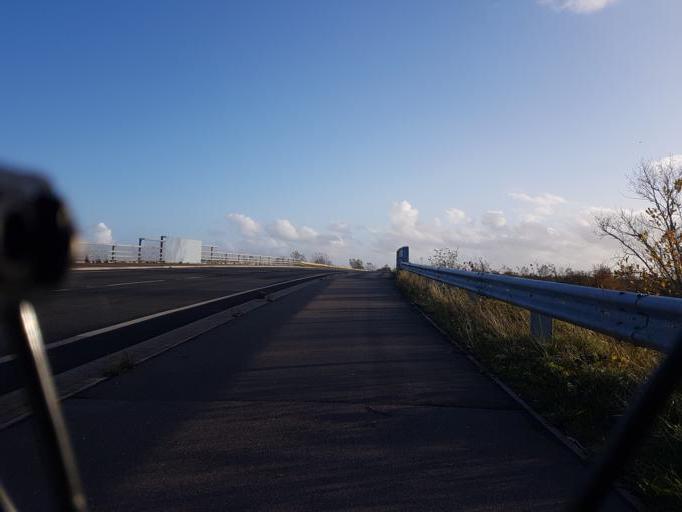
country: GB
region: England
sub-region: Kent
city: Sittingbourne
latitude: 51.3575
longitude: 0.7528
